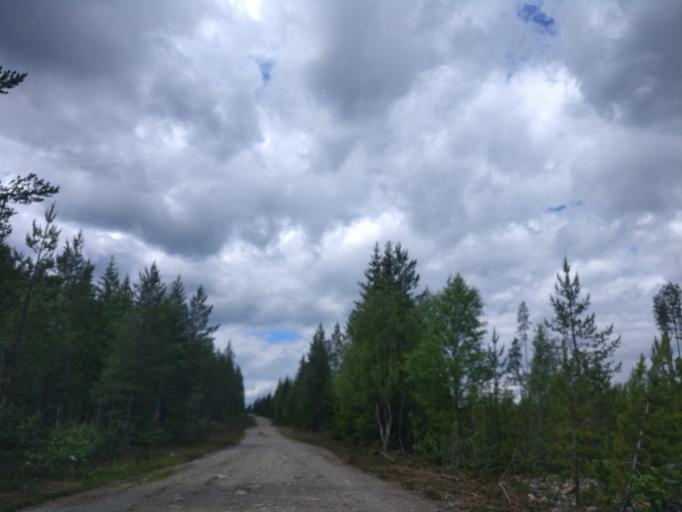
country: SE
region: Jaemtland
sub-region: Harjedalens Kommun
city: Sveg
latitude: 62.1965
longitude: 13.4128
